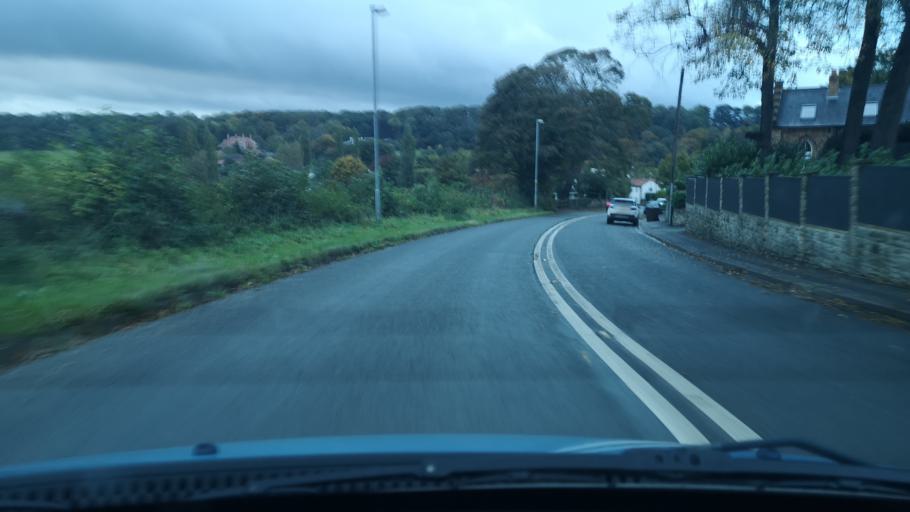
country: GB
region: England
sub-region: City and Borough of Wakefield
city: Darrington
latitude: 53.6474
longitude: -1.2643
